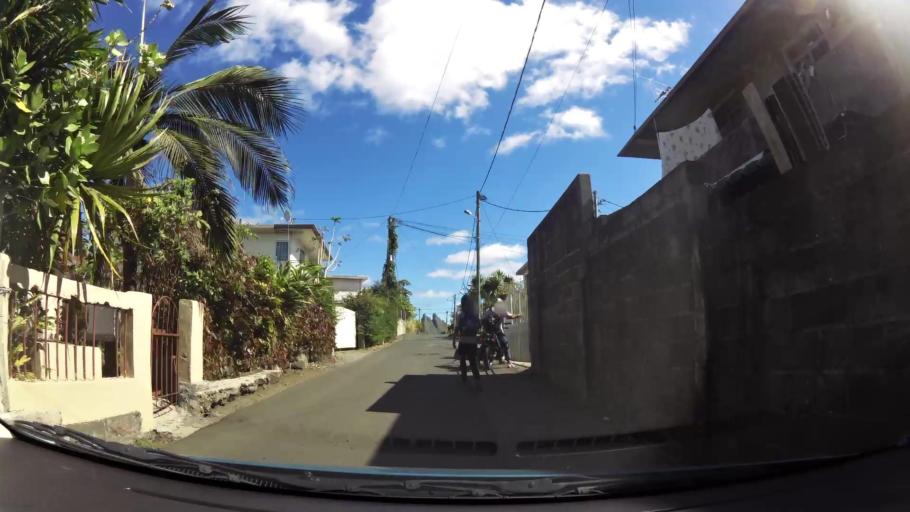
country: MU
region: Plaines Wilhems
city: Vacoas
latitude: -20.3064
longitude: 57.4808
